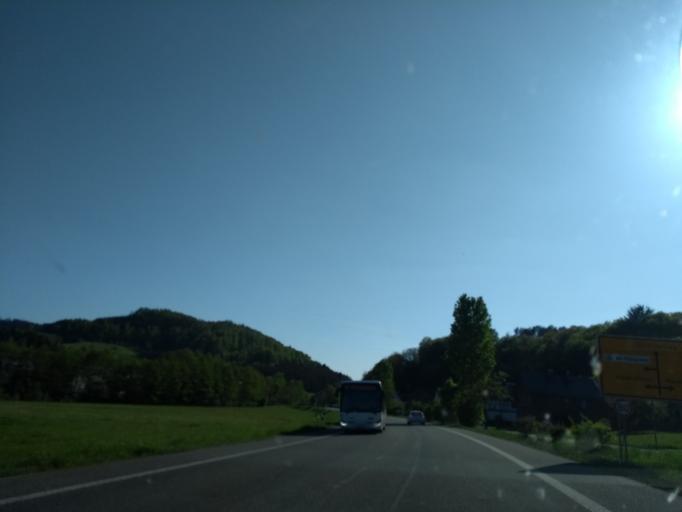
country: DE
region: Hesse
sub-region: Regierungsbezirk Giessen
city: Breidenbach
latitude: 50.8733
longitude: 8.4426
